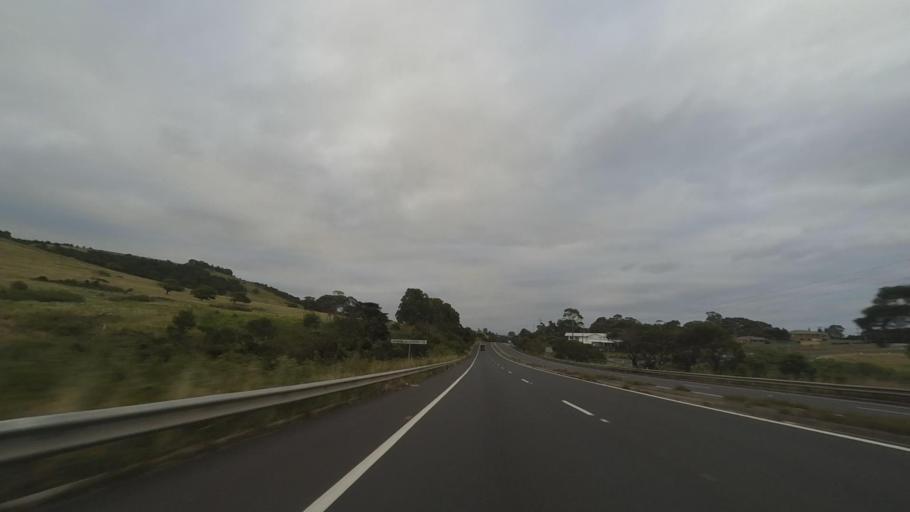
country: AU
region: New South Wales
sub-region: Kiama
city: Kiama
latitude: -34.6910
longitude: 150.8440
